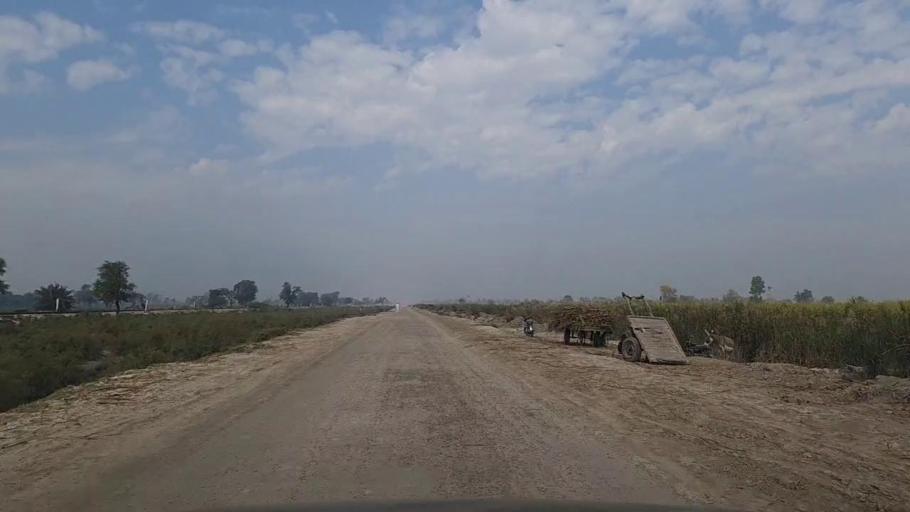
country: PK
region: Sindh
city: Daur
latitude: 26.3752
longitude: 68.3570
